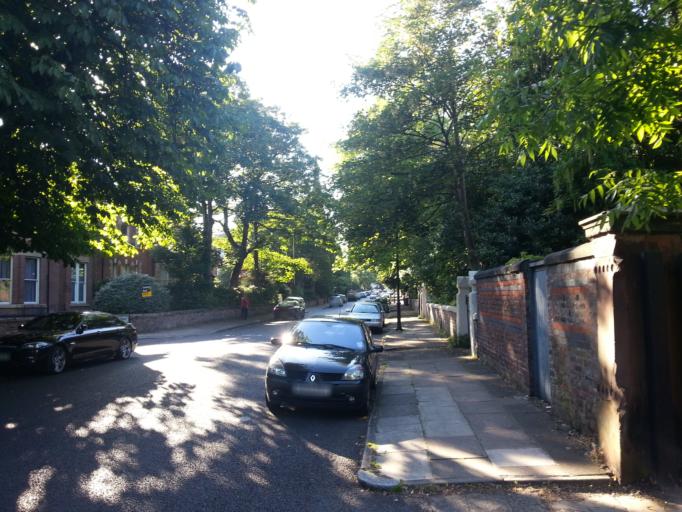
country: GB
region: England
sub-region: Liverpool
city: Liverpool
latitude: 53.3838
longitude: -2.9462
